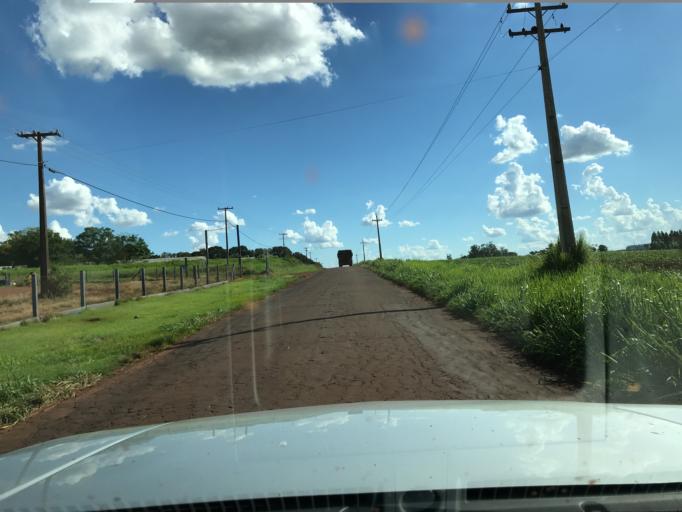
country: BR
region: Parana
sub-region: Palotina
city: Palotina
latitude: -24.2595
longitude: -53.7992
